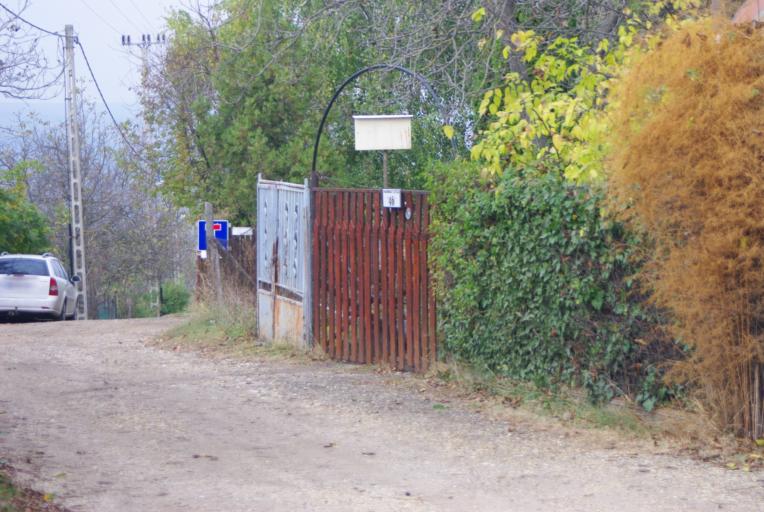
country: HU
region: Pest
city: Isaszeg
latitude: 47.5142
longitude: 19.3846
